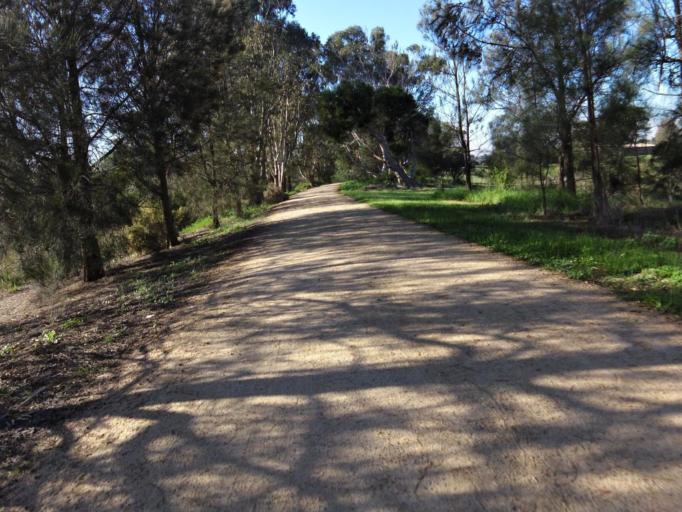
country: AU
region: Victoria
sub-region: Kingston
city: Mordialloc
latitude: -38.0106
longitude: 145.0982
